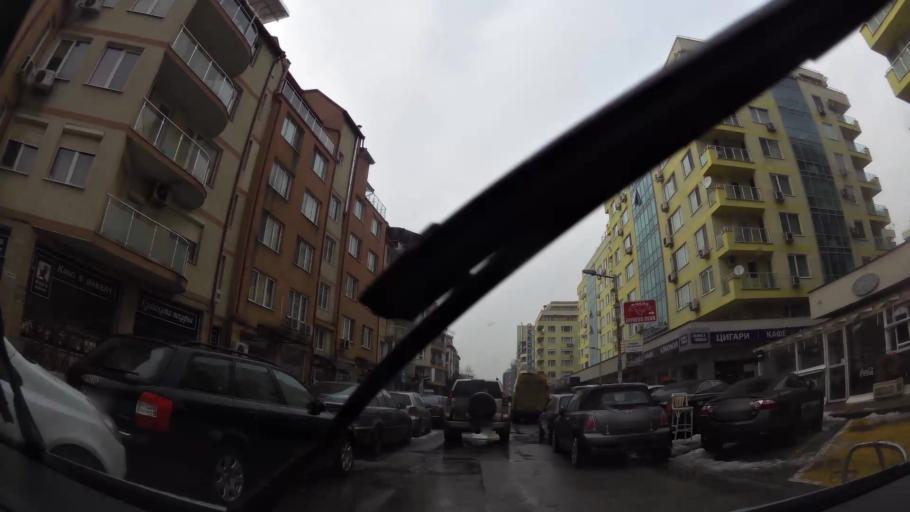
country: BG
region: Sofia-Capital
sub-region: Stolichna Obshtina
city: Sofia
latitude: 42.6642
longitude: 23.2846
